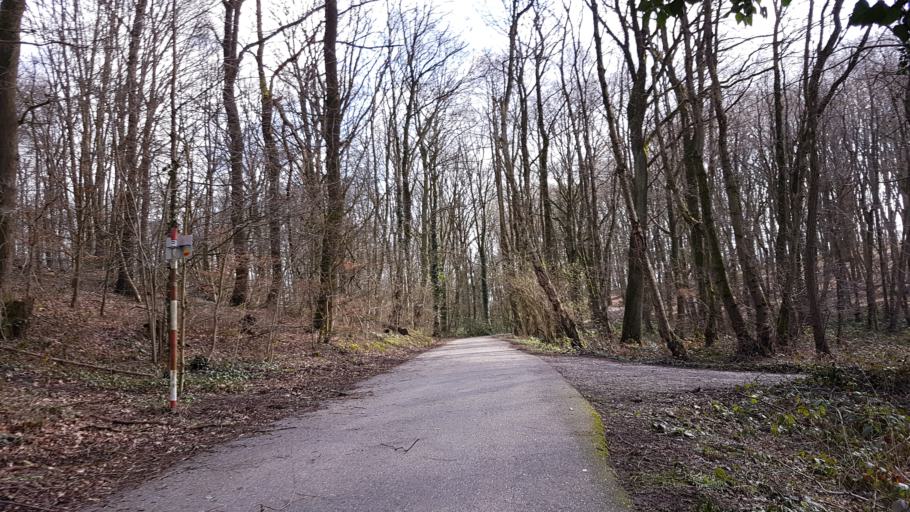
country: DE
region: North Rhine-Westphalia
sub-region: Regierungsbezirk Dusseldorf
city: Niederkruchten
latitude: 51.2187
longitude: 6.2293
